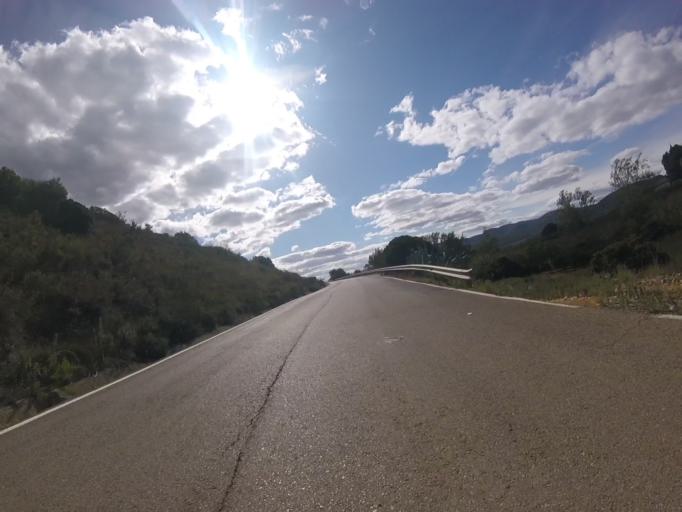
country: ES
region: Valencia
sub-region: Provincia de Castello
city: Cuevas de Vinroma
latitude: 40.3688
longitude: 0.1218
